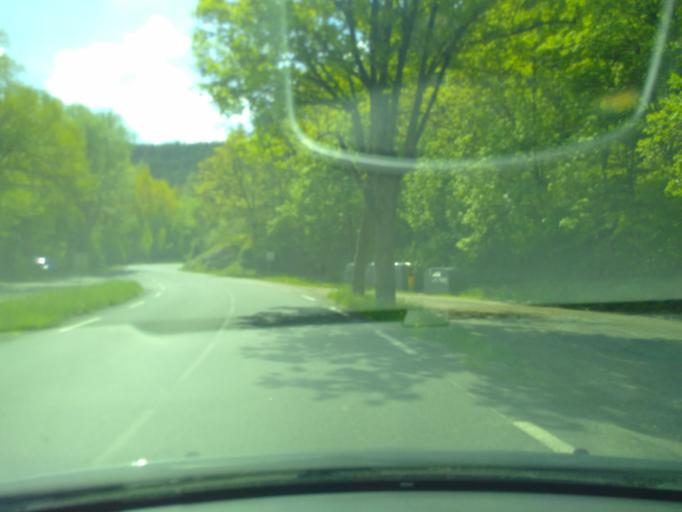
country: FR
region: Rhone-Alpes
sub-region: Departement de la Drome
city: Die
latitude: 44.6005
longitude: 5.4582
